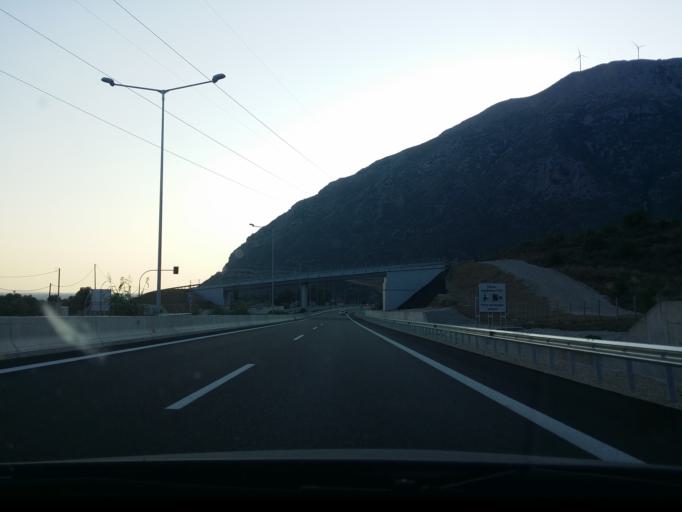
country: GR
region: West Greece
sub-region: Nomos Aitolias kai Akarnanias
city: Antirrio
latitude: 38.3540
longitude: 21.7132
